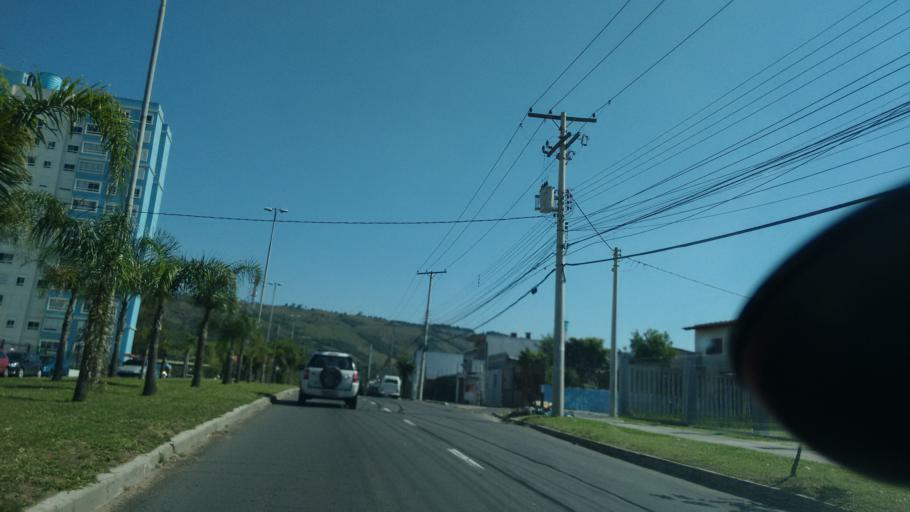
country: BR
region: Rio Grande do Sul
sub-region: Cachoeirinha
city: Cachoeirinha
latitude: -30.0346
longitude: -51.1217
